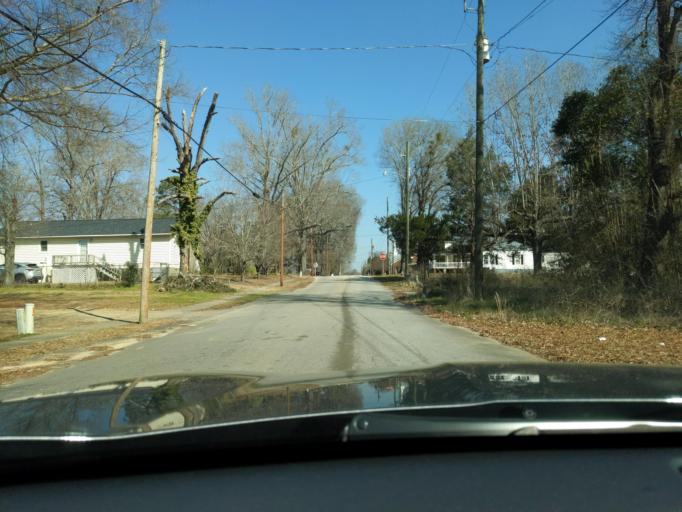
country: US
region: South Carolina
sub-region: Abbeville County
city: Calhoun Falls
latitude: 34.0909
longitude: -82.5920
